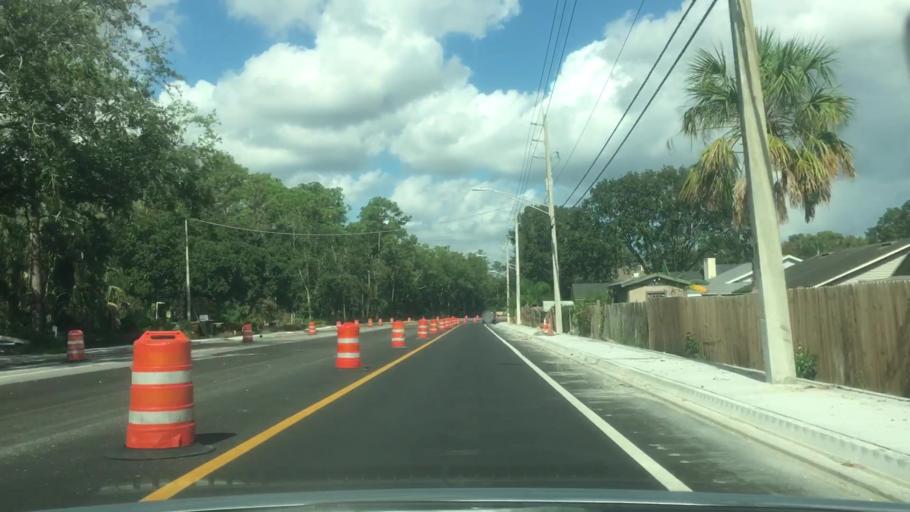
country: US
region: Florida
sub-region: Duval County
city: Atlantic Beach
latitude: 30.3263
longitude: -81.4719
